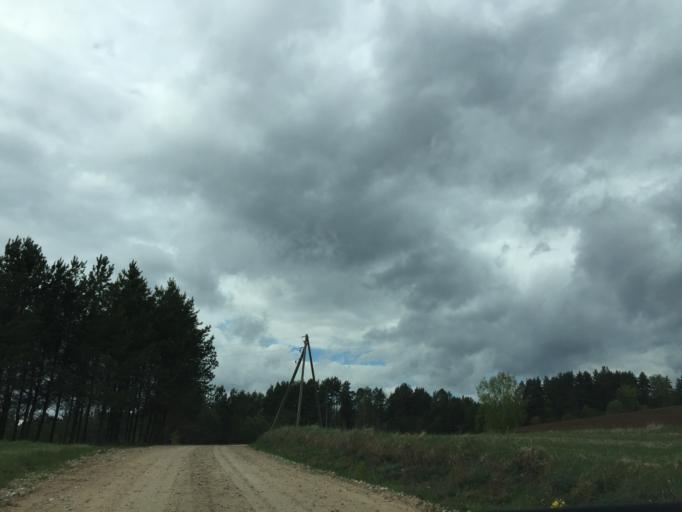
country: LV
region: Salaspils
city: Salaspils
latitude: 56.7930
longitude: 24.3113
